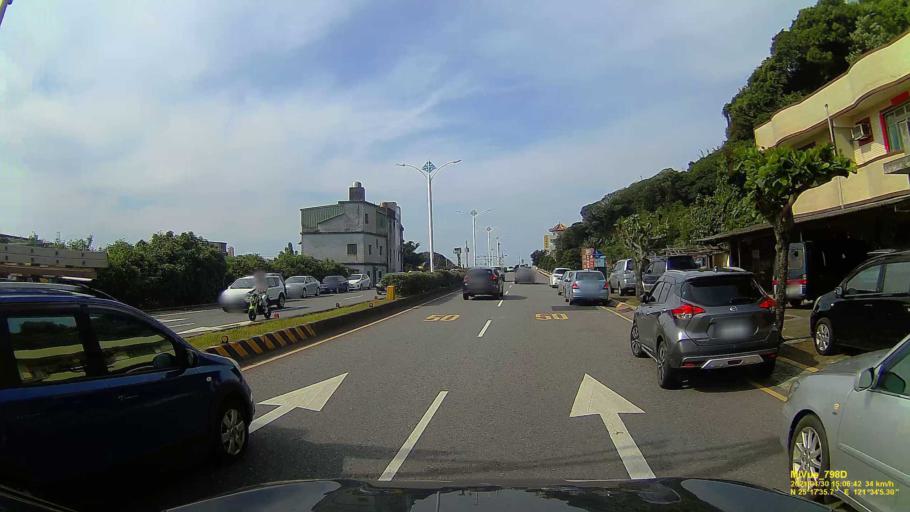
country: TW
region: Taiwan
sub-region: Keelung
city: Keelung
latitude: 25.2934
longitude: 121.5682
